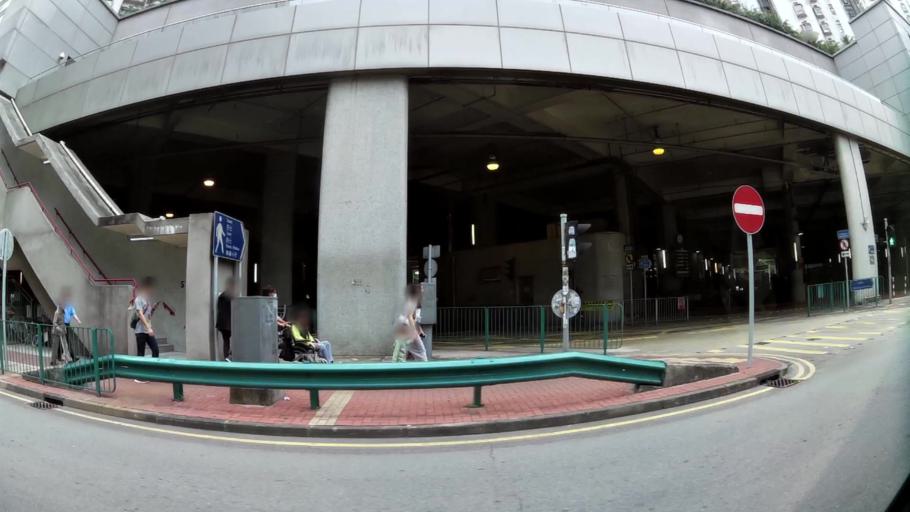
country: HK
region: Tuen Mun
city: Tuen Mun
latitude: 22.3730
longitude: 113.9667
